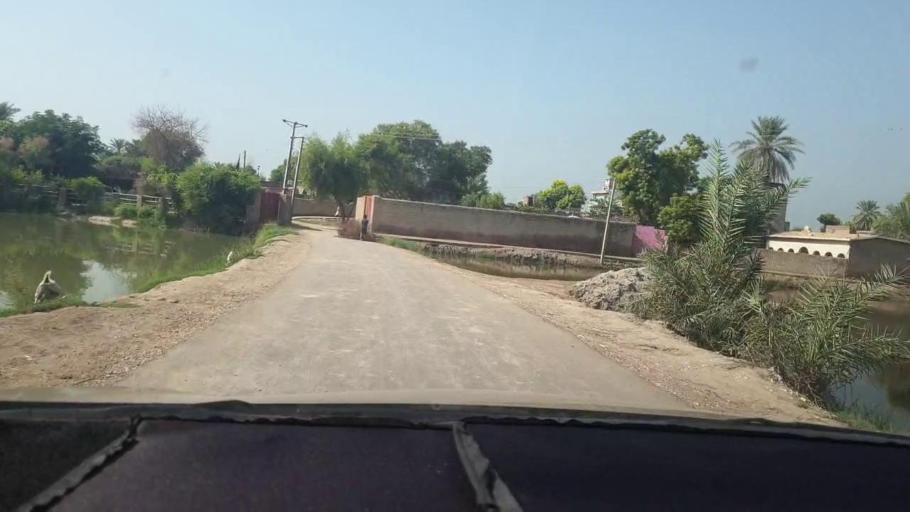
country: PK
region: Sindh
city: Kambar
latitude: 27.5731
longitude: 68.0744
